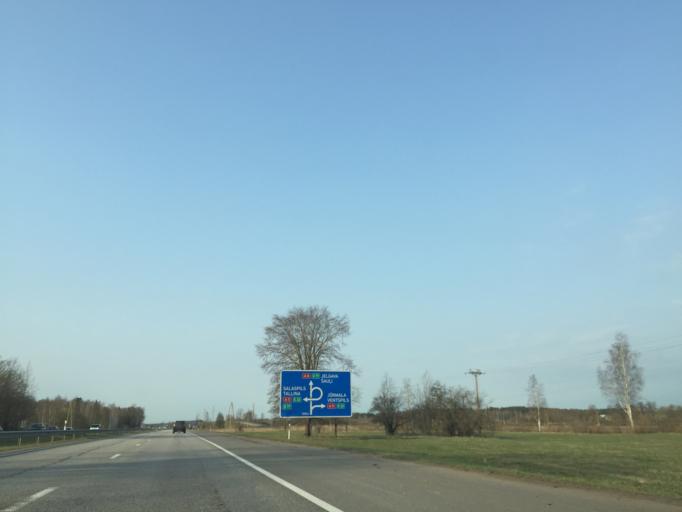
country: LV
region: Marupe
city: Marupe
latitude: 56.8404
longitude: 24.0499
